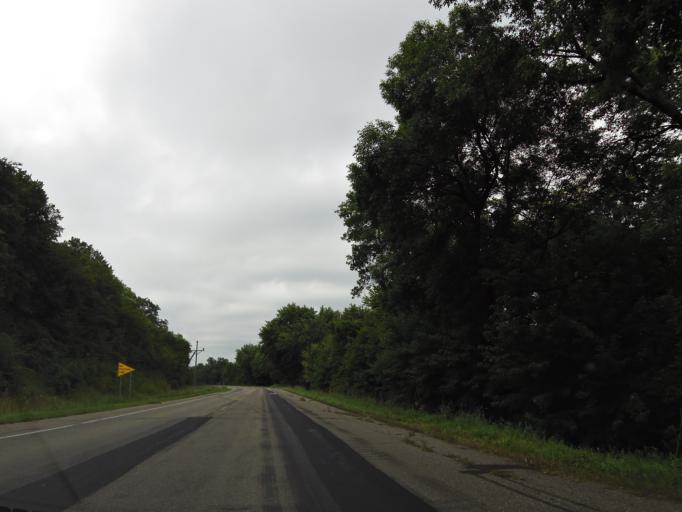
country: US
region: Minnesota
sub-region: Chippewa County
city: Montevideo
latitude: 44.8934
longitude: -95.6660
